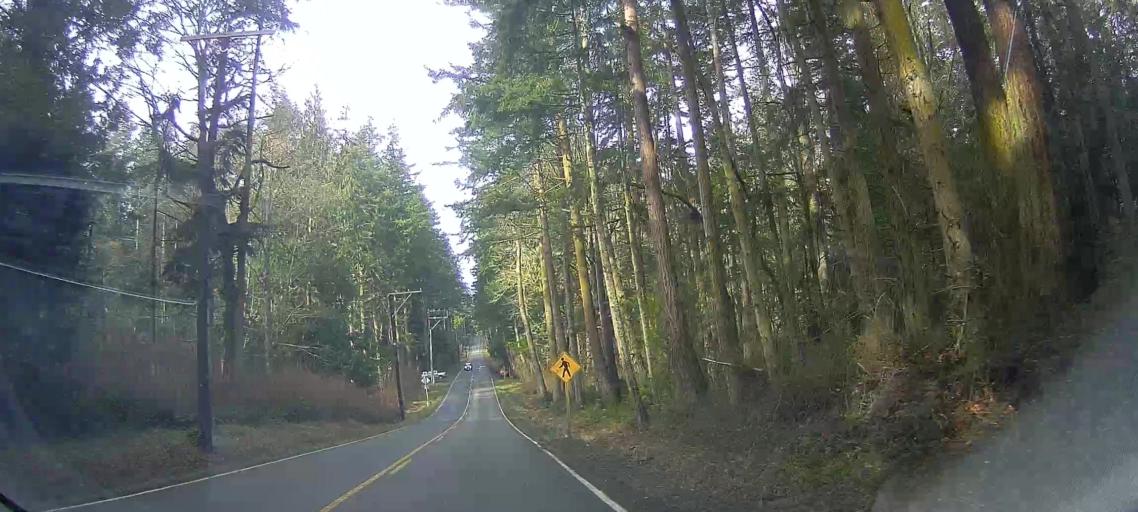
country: US
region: Washington
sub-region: Island County
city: Camano
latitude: 48.1414
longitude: -122.5066
